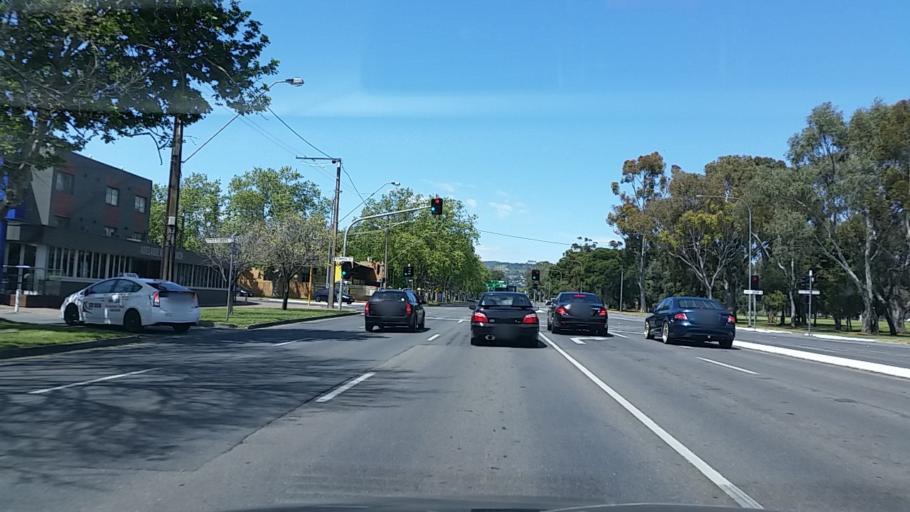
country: AU
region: South Australia
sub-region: Adelaide
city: Adelaide
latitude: -34.9247
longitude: 138.6187
